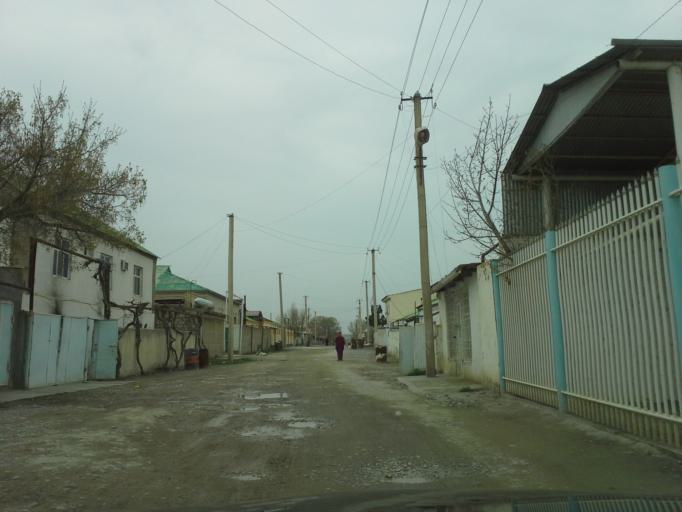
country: TM
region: Ahal
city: Abadan
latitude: 37.9760
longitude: 58.2191
